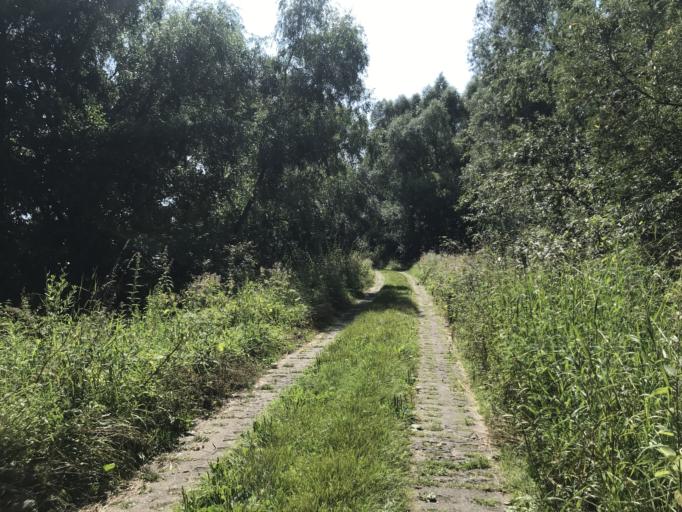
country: PL
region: Pomeranian Voivodeship
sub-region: Gdansk
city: Gdansk
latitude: 54.3186
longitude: 18.6745
